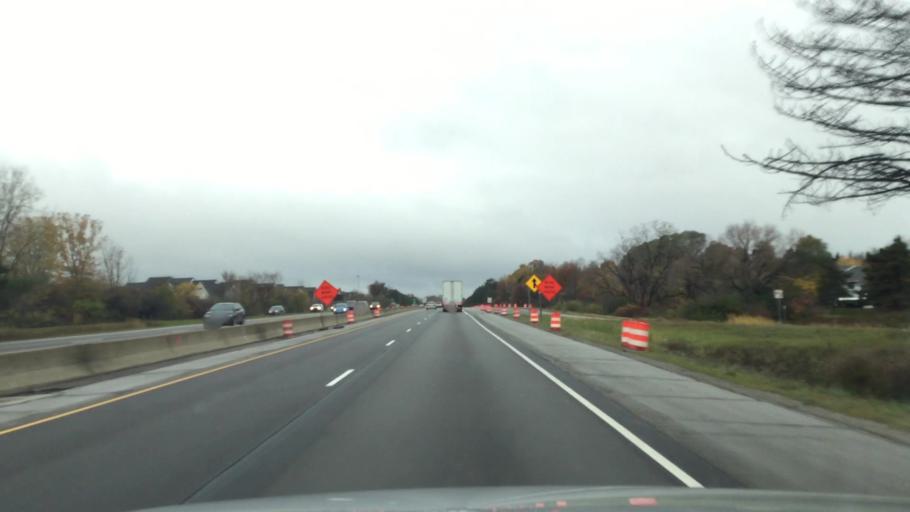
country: US
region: Michigan
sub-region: Washtenaw County
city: Ann Arbor
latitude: 42.2477
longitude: -83.7660
